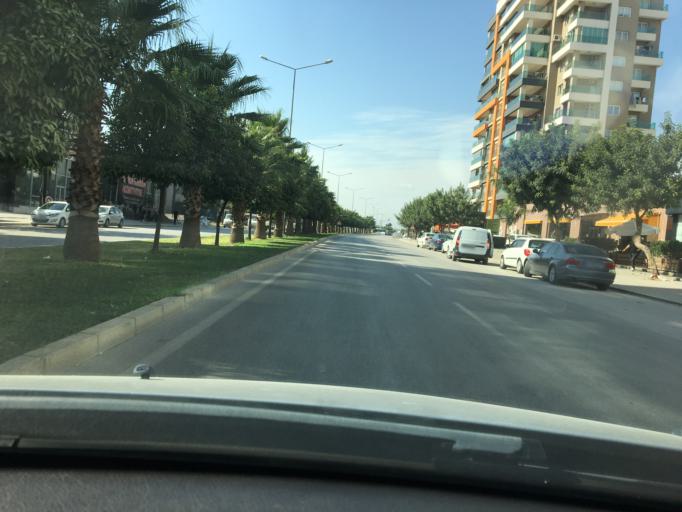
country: TR
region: Adana
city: Seyhan
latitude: 37.0228
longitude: 35.2567
